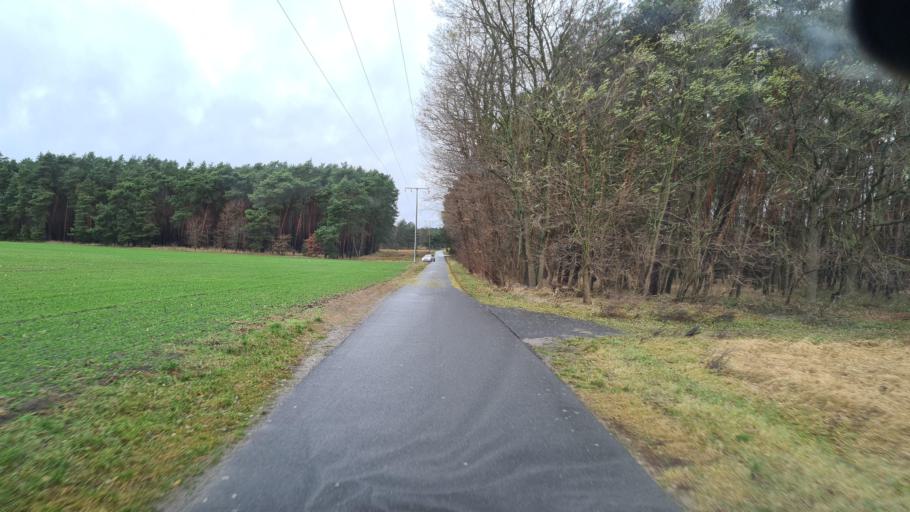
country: DE
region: Brandenburg
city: Tauche
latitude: 52.0875
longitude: 14.1449
